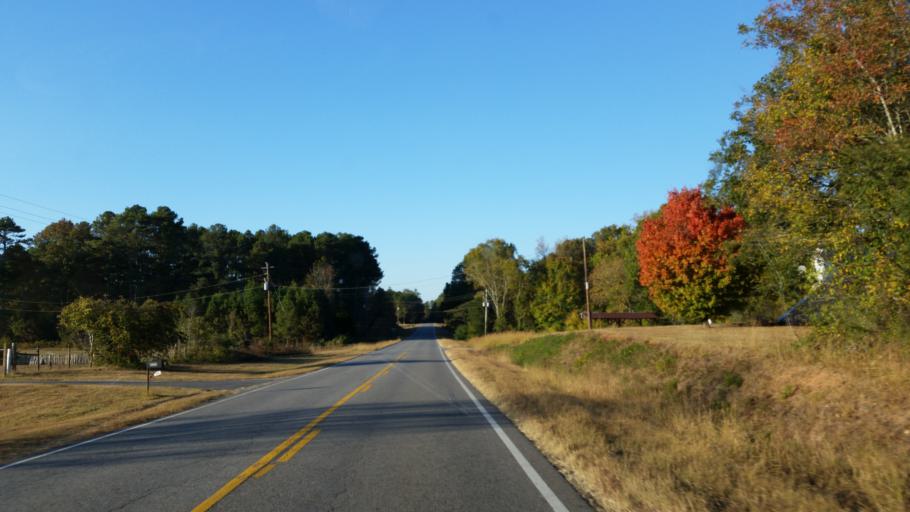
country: US
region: Georgia
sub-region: Bartow County
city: Adairsville
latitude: 34.3342
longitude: -84.9354
